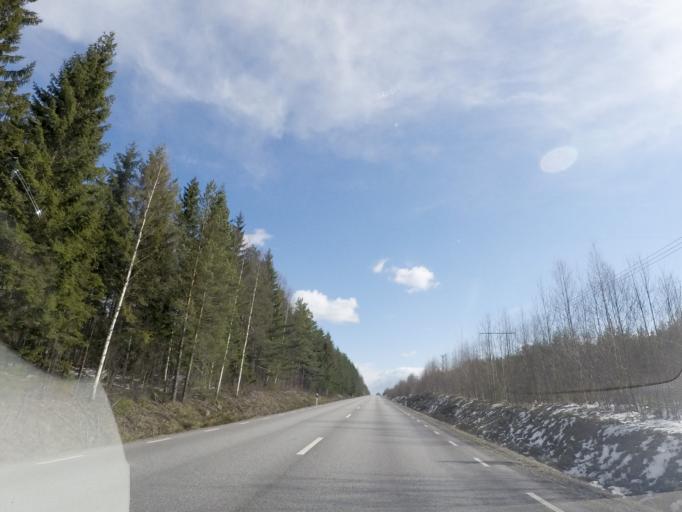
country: SE
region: Vaestmanland
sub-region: Skinnskattebergs Kommun
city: Skinnskatteberg
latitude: 59.8564
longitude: 15.6588
